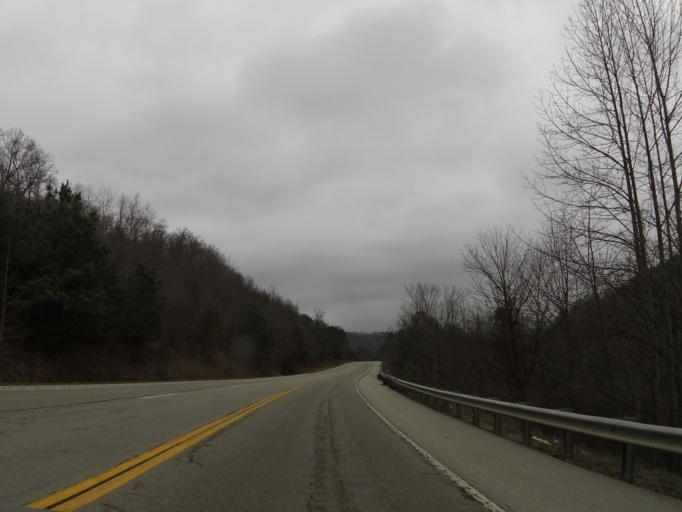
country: US
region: Tennessee
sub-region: Scott County
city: Huntsville
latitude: 36.3745
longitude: -84.5715
